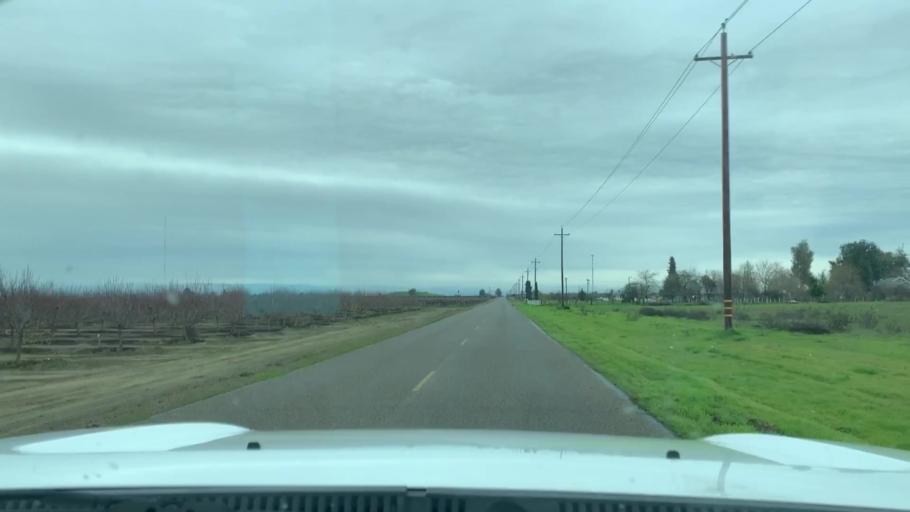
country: US
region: California
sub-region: Fresno County
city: Caruthers
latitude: 36.5474
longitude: -119.7700
